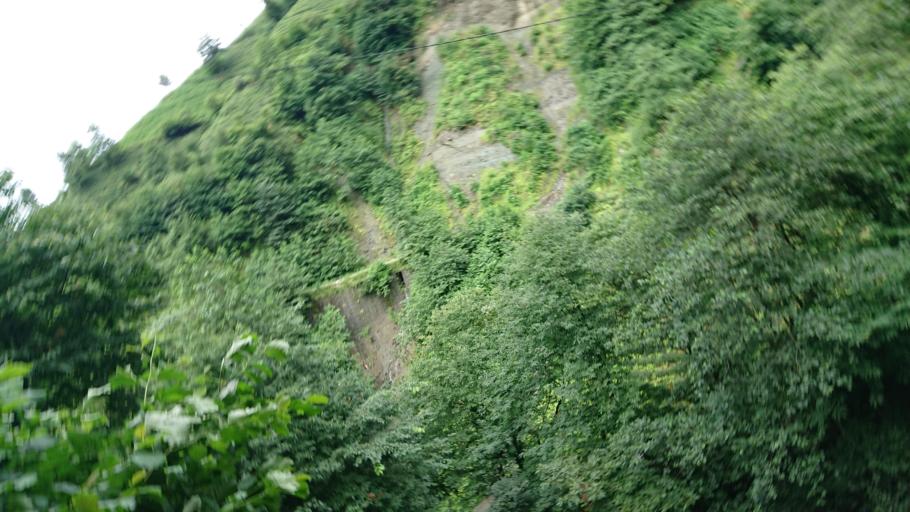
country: TR
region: Rize
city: Rize
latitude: 40.9720
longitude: 40.4875
